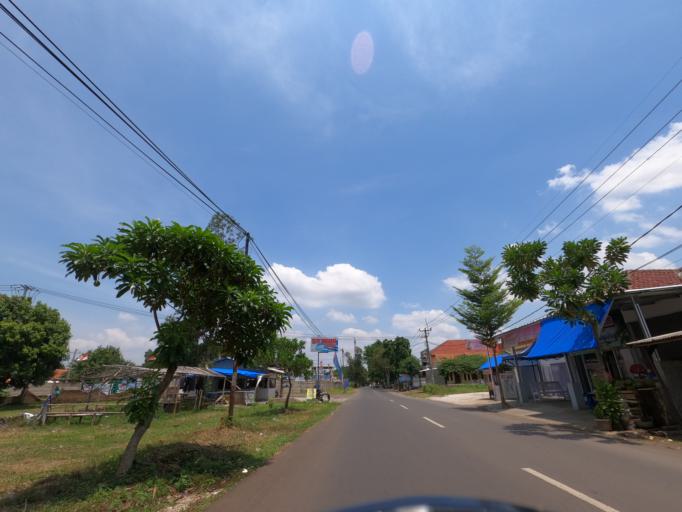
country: ID
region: West Java
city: Pamanukan
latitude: -6.5447
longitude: 107.7670
